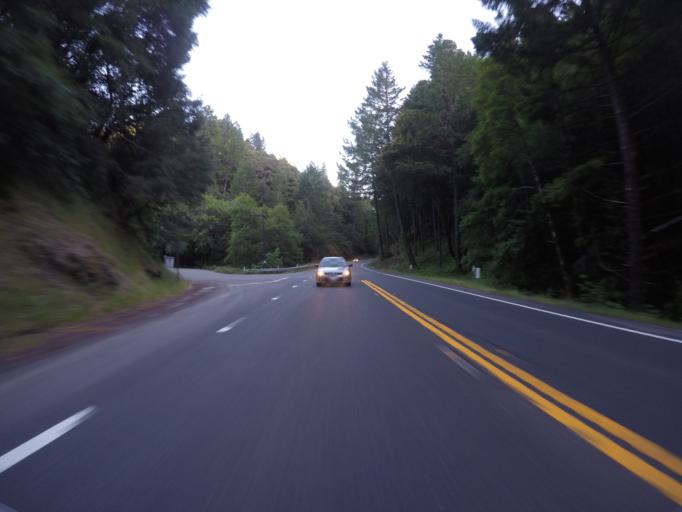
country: US
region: California
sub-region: Mendocino County
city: Laytonville
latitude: 39.7982
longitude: -123.5425
